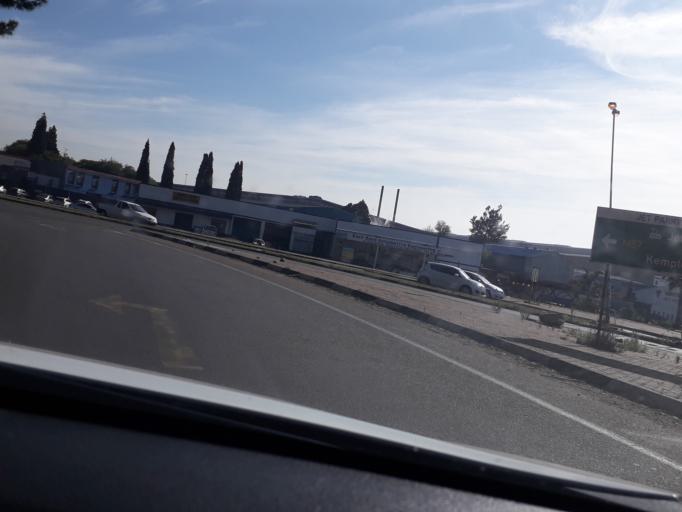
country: ZA
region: Gauteng
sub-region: Ekurhuleni Metropolitan Municipality
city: Boksburg
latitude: -26.1720
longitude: 28.2040
